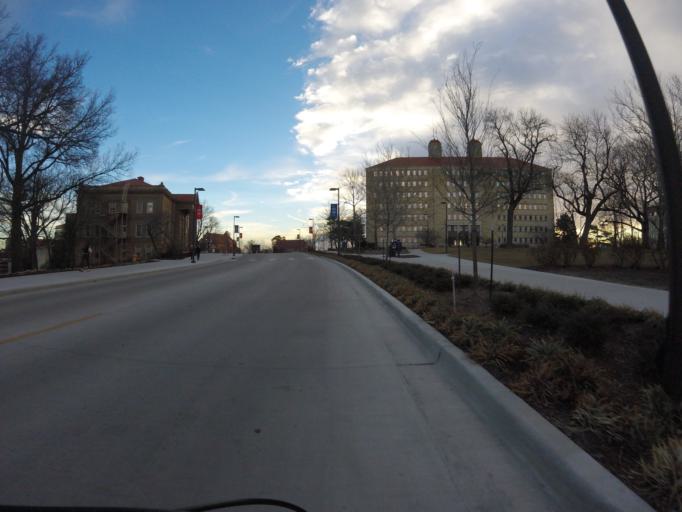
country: US
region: Kansas
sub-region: Douglas County
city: Lawrence
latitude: 38.9523
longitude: -95.2607
